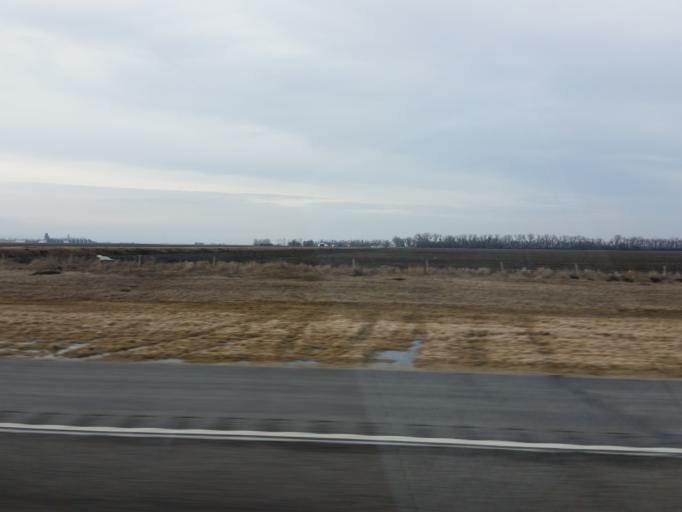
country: US
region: North Dakota
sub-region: Cass County
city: Casselton
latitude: 46.8768
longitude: -97.1781
